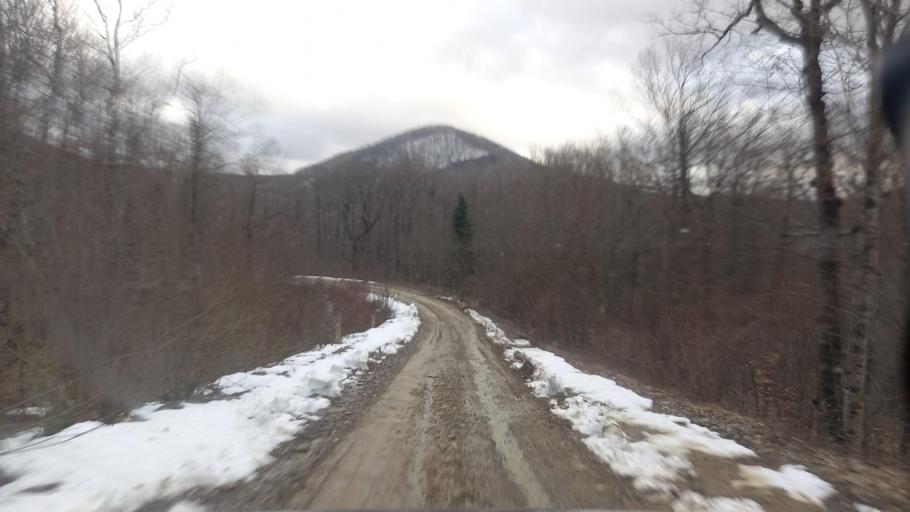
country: RU
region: Krasnodarskiy
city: Dzhubga
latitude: 44.5077
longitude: 38.7746
